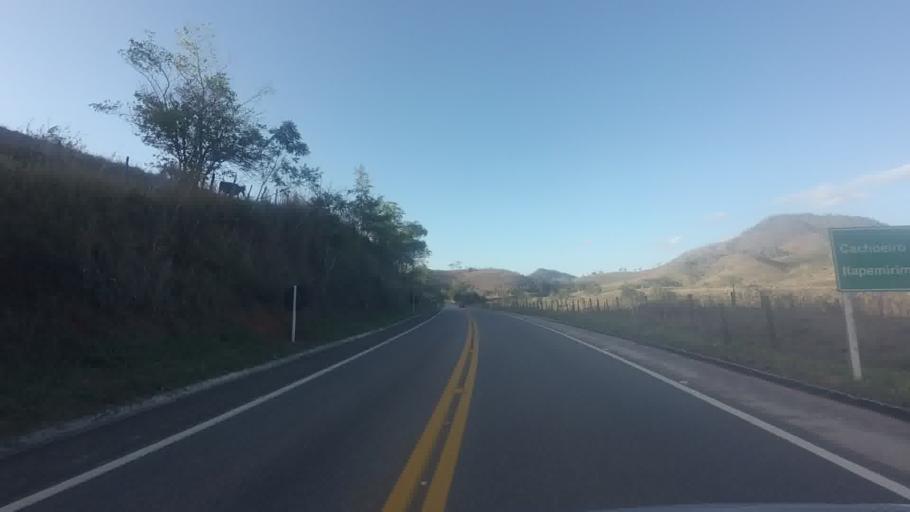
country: BR
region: Espirito Santo
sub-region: Jeronimo Monteiro
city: Jeronimo Monteiro
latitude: -20.8836
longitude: -41.2697
